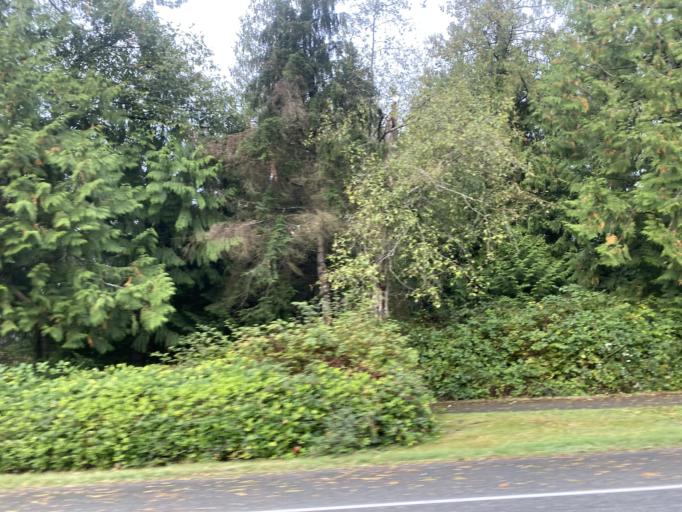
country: US
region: Washington
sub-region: Island County
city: Langley
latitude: 48.0133
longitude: -122.4096
